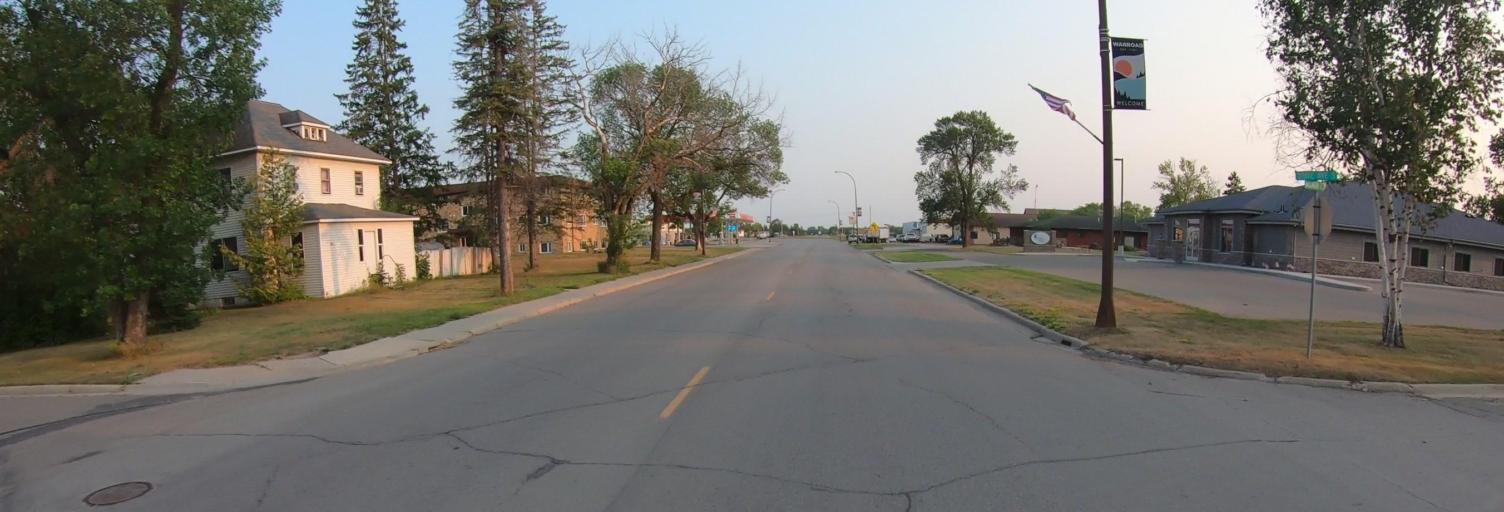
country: US
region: Minnesota
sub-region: Roseau County
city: Warroad
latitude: 48.9012
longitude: -95.3201
